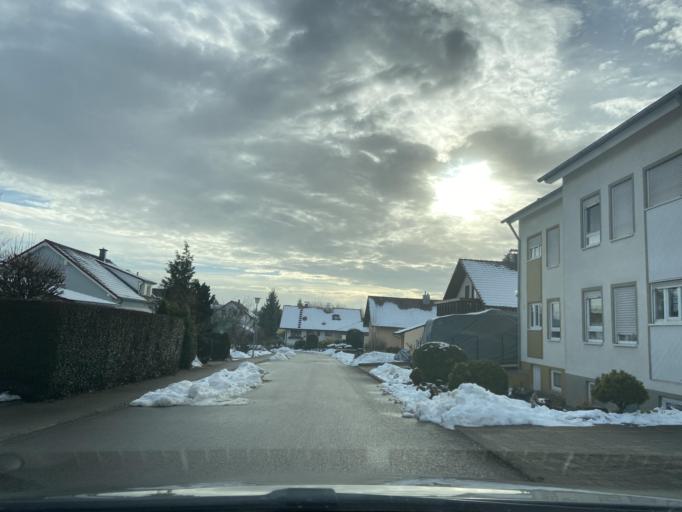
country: DE
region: Baden-Wuerttemberg
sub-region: Tuebingen Region
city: Neufra
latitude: 48.2426
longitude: 9.2038
